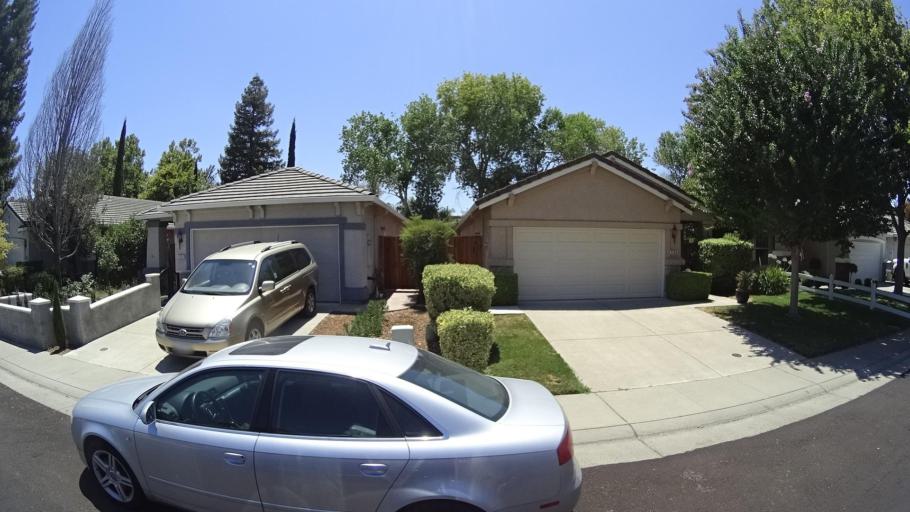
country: US
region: California
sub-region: Placer County
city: Rocklin
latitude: 38.8169
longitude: -121.2574
